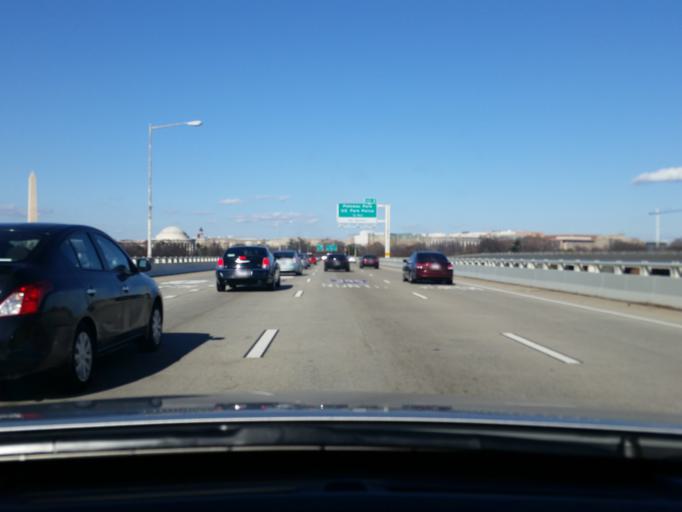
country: US
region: Washington, D.C.
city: Washington, D.C.
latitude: 38.8749
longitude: -77.0400
